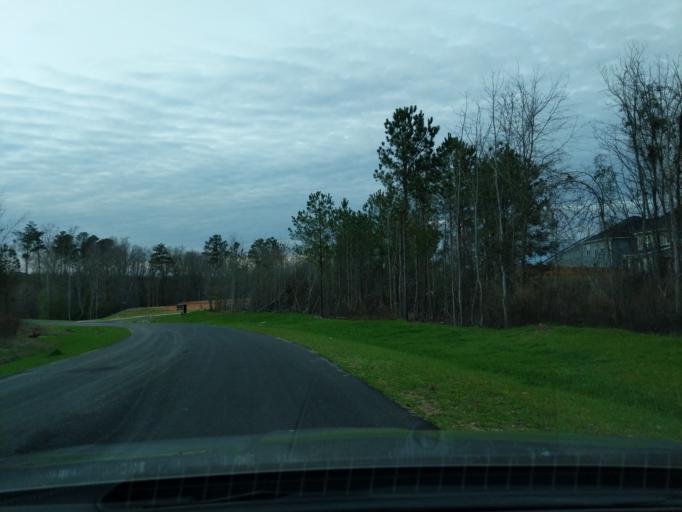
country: US
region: Georgia
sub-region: Columbia County
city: Grovetown
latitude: 33.4678
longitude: -82.2012
